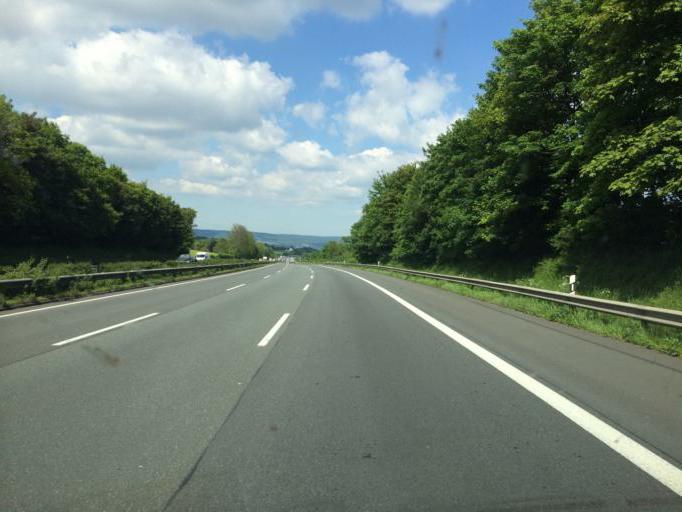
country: DE
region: North Rhine-Westphalia
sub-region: Regierungsbezirk Detmold
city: Vlotho
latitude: 52.1592
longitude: 8.8119
